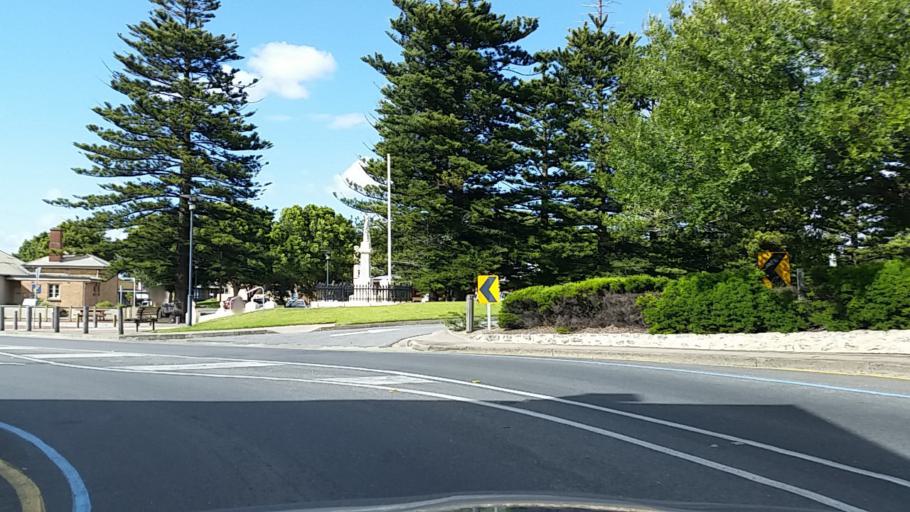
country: AU
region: South Australia
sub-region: Alexandrina
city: Goolwa
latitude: -35.5038
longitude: 138.7842
